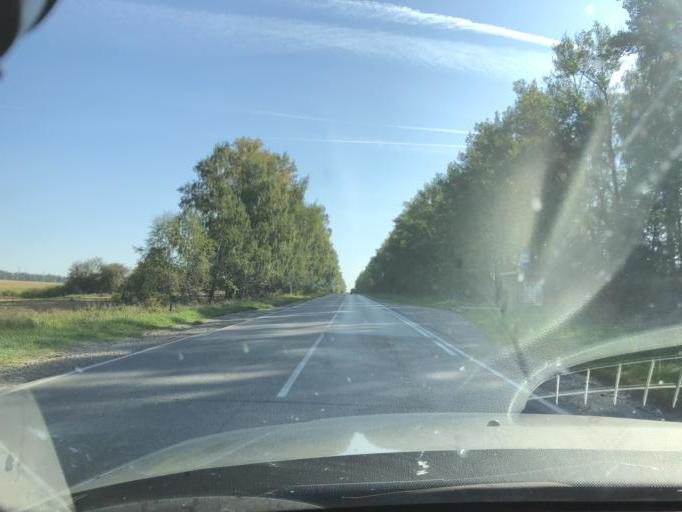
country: RU
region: Tula
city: Yasnogorsk
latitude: 54.4689
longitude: 37.6391
